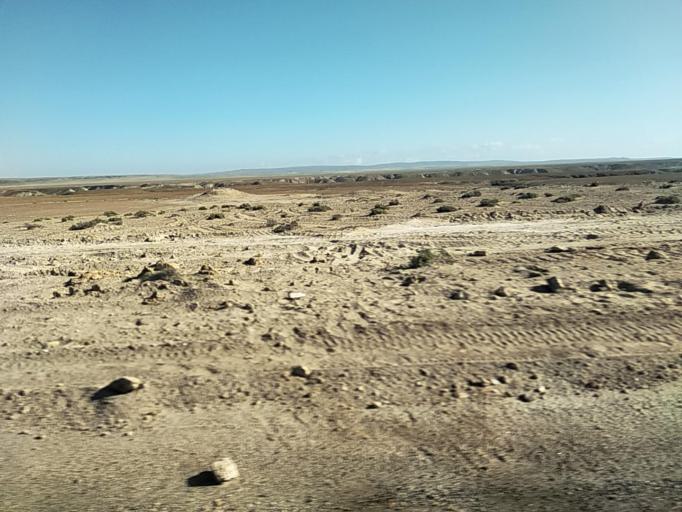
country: CL
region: Atacama
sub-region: Provincia de Copiapo
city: Copiapo
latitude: -27.3186
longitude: -70.8283
